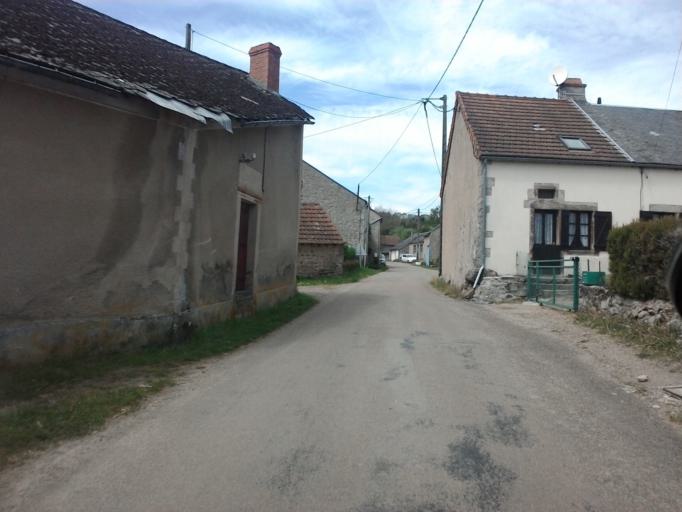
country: FR
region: Bourgogne
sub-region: Departement de la Nievre
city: Lormes
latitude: 47.3017
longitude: 3.9000
